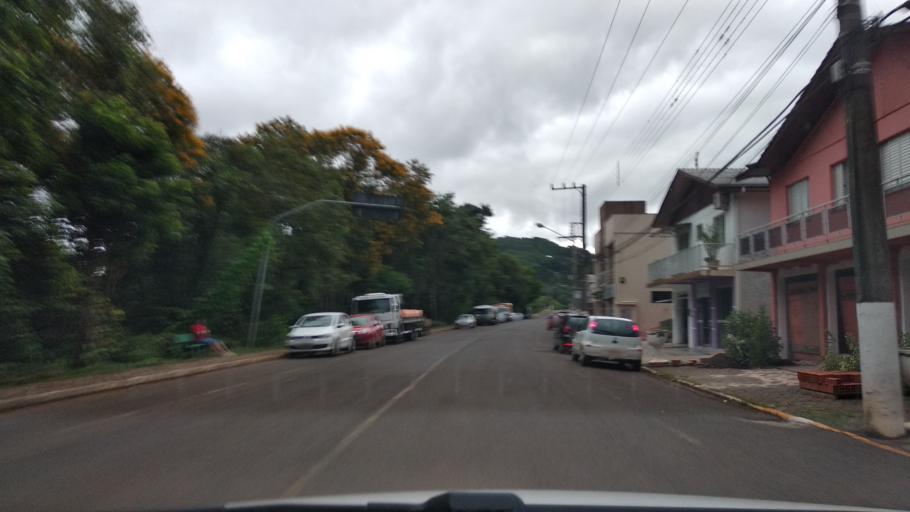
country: BR
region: Santa Catarina
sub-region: Videira
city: Videira
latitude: -27.0456
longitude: -51.2274
